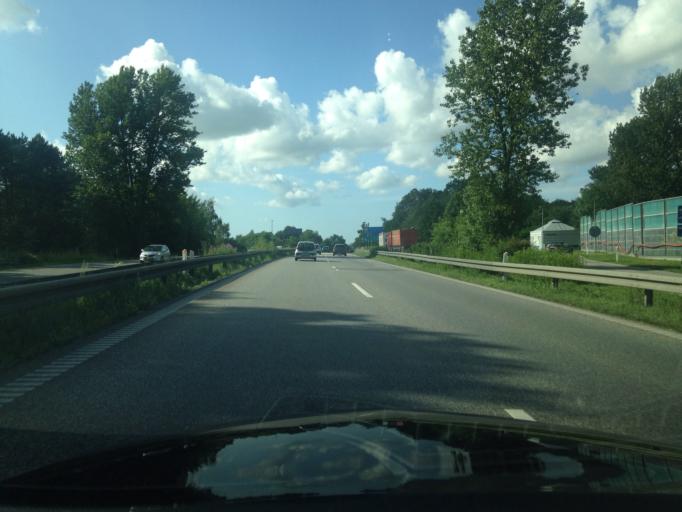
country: DK
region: Capital Region
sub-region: Horsholm Kommune
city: Horsholm
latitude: 55.8638
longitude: 12.4872
